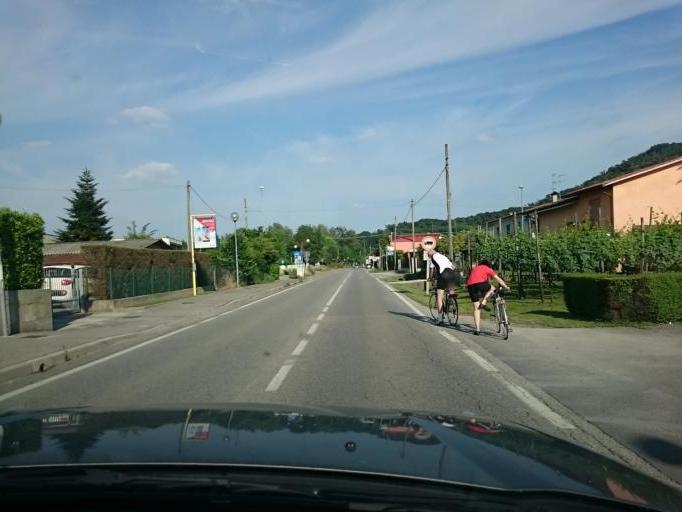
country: IT
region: Veneto
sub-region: Provincia di Padova
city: Torreglia
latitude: 45.3325
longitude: 11.7584
